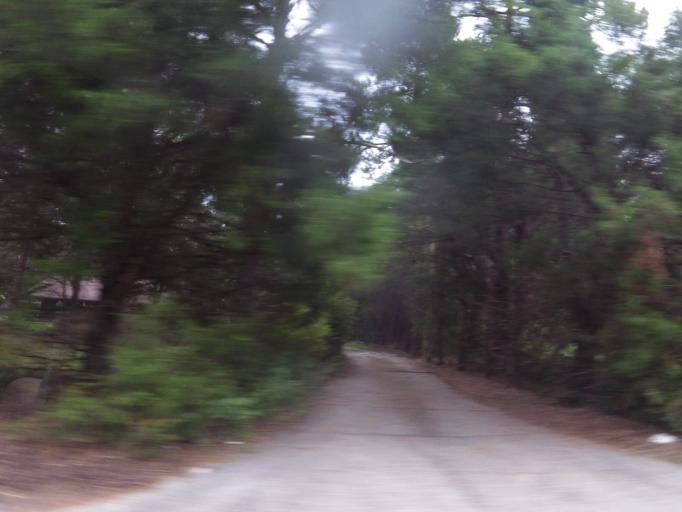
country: US
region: Florida
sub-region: Clay County
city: Middleburg
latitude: 30.1114
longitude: -81.9491
